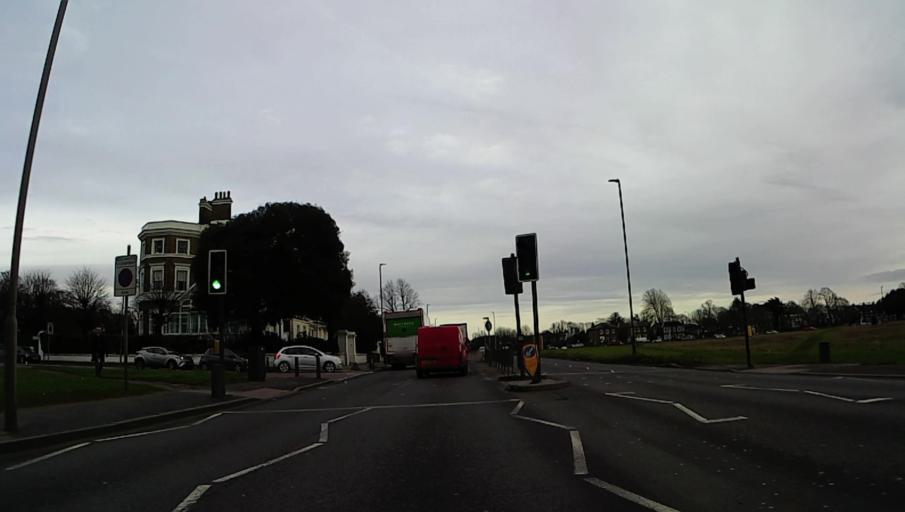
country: GB
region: England
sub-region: Greater London
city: Blackheath
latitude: 51.4733
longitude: 0.0121
